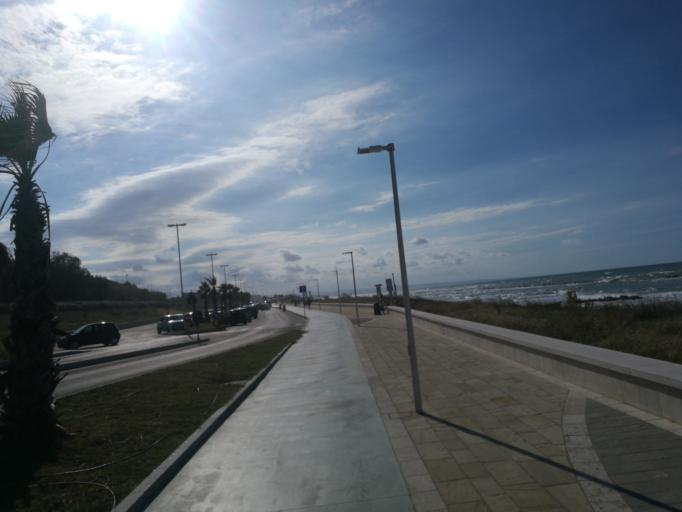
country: IT
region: Molise
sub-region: Provincia di Campobasso
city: Termoli
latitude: 42.0066
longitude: 14.9774
